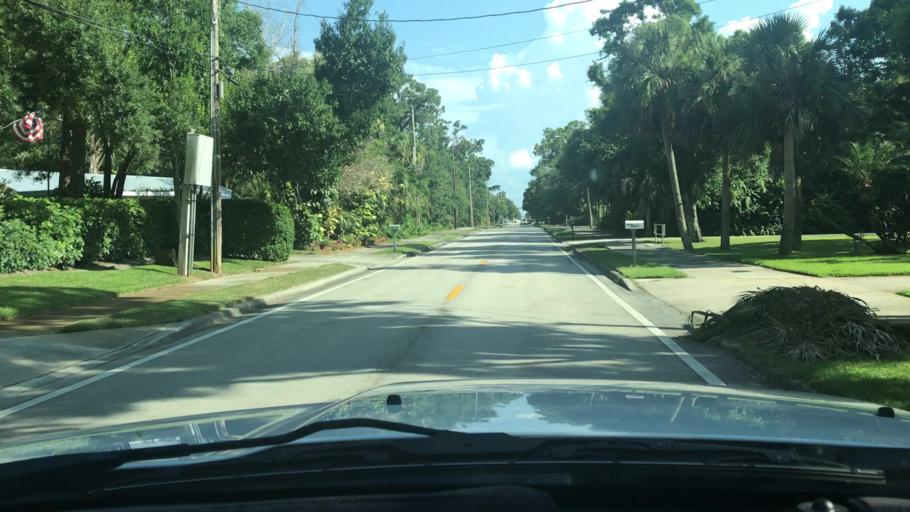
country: US
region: Florida
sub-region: Indian River County
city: Vero Beach
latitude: 27.6418
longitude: -80.4138
